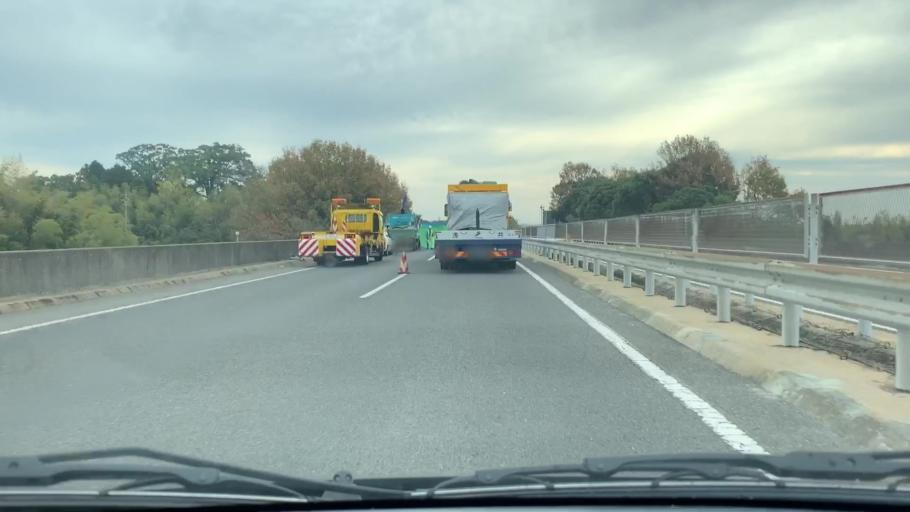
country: JP
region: Saga Prefecture
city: Saga-shi
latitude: 33.3074
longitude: 130.2283
